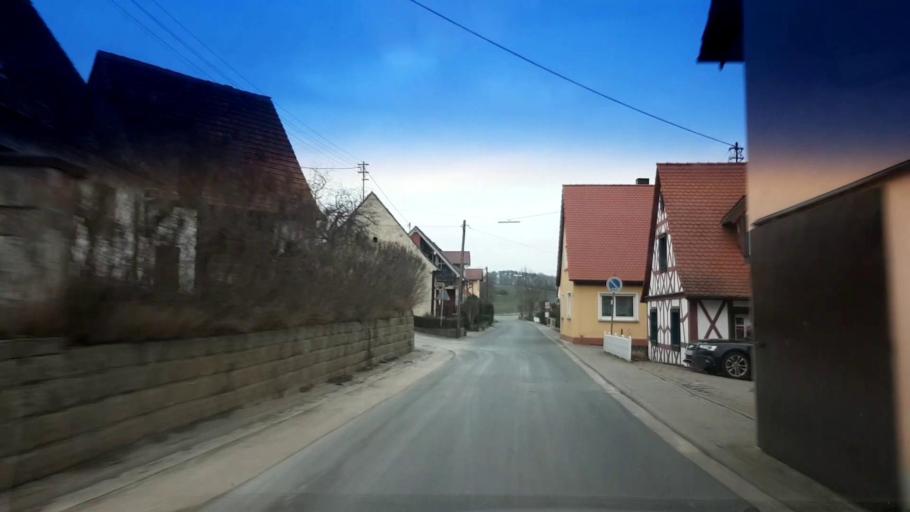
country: DE
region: Bavaria
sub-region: Upper Franconia
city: Hallerndorf
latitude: 49.7620
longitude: 10.9850
